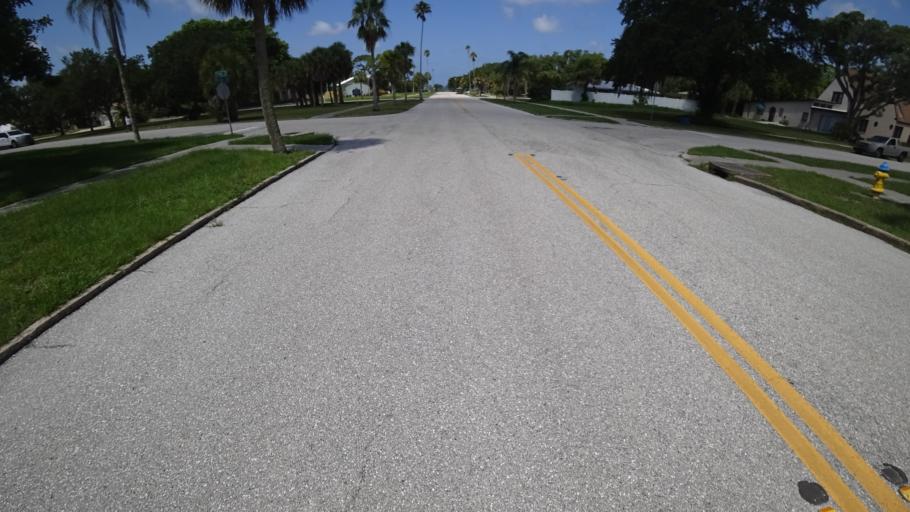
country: US
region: Florida
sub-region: Manatee County
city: Whitfield
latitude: 27.4086
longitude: -82.5725
